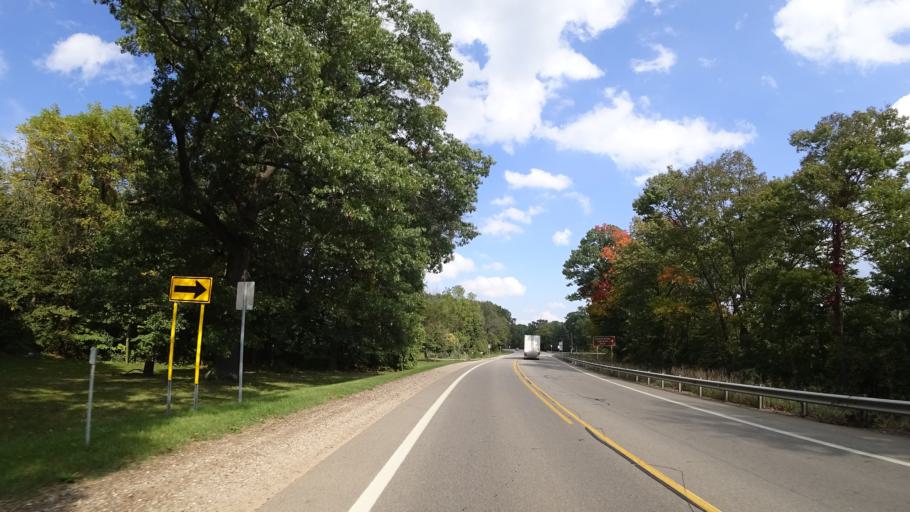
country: US
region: Michigan
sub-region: Saint Joseph County
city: Centreville
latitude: 41.9655
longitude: -85.5714
